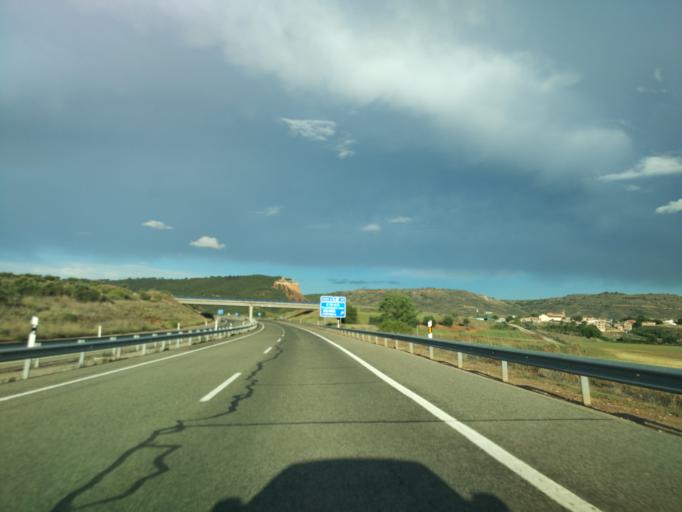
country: ES
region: Castille-La Mancha
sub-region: Provincia de Guadalajara
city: Guadalajara
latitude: 40.6595
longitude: -3.1371
